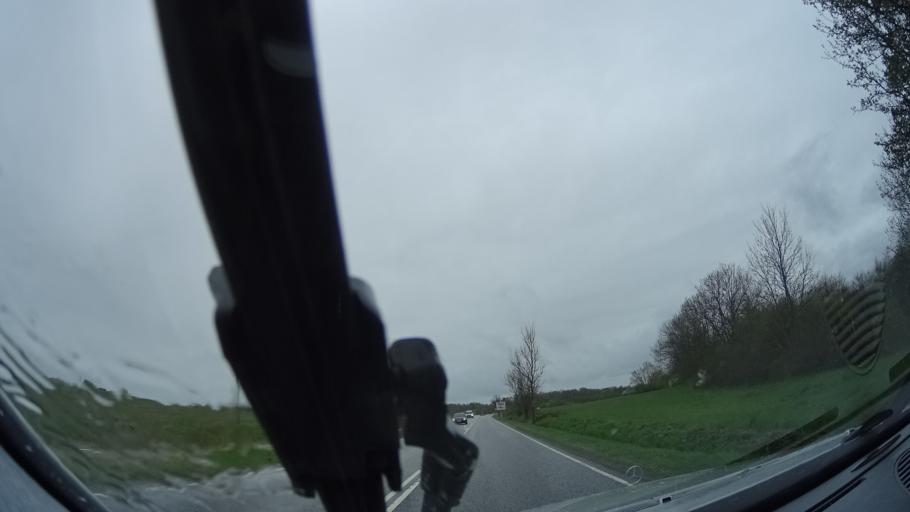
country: DK
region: Zealand
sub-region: Lejre Kommune
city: Ejby
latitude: 55.6741
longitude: 11.8326
